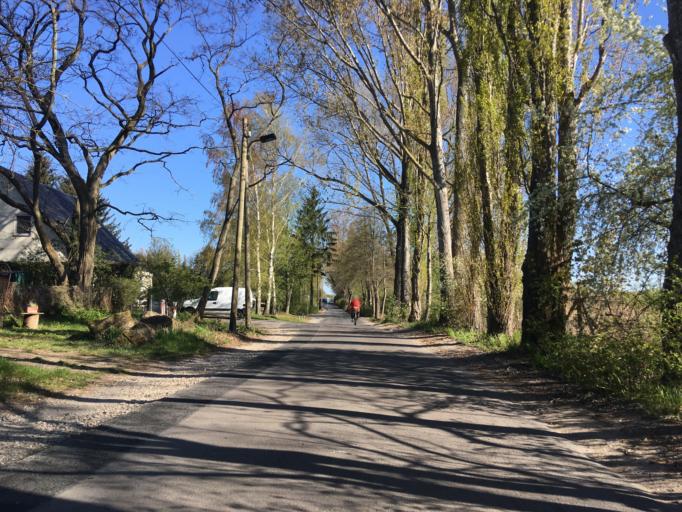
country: DE
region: Berlin
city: Wartenberg
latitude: 52.5836
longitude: 13.4981
